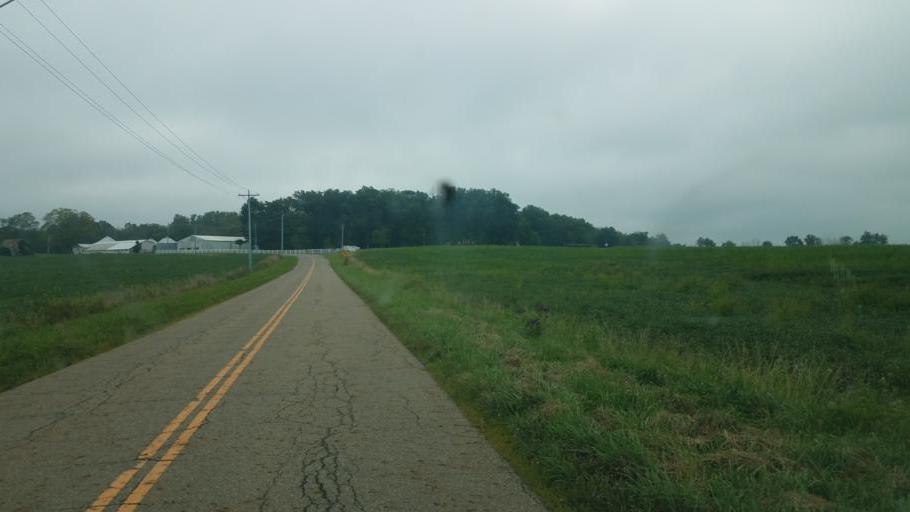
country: US
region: Ohio
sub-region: Licking County
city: Utica
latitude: 40.2896
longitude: -82.4303
